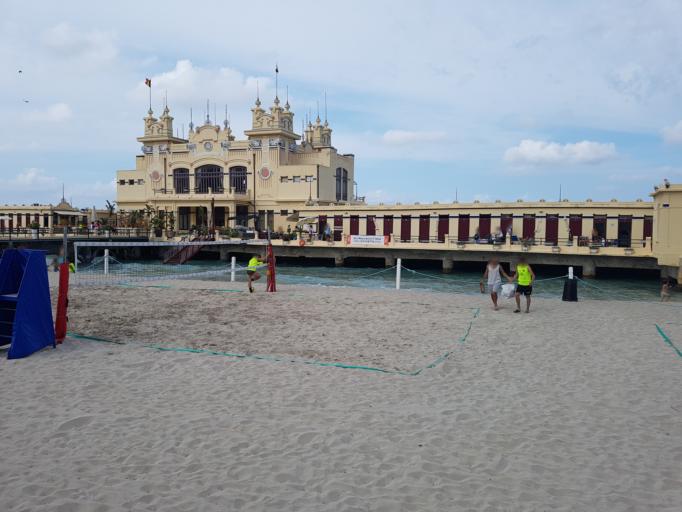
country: IT
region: Sicily
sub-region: Palermo
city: Palermo
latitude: 38.2021
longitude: 13.3268
